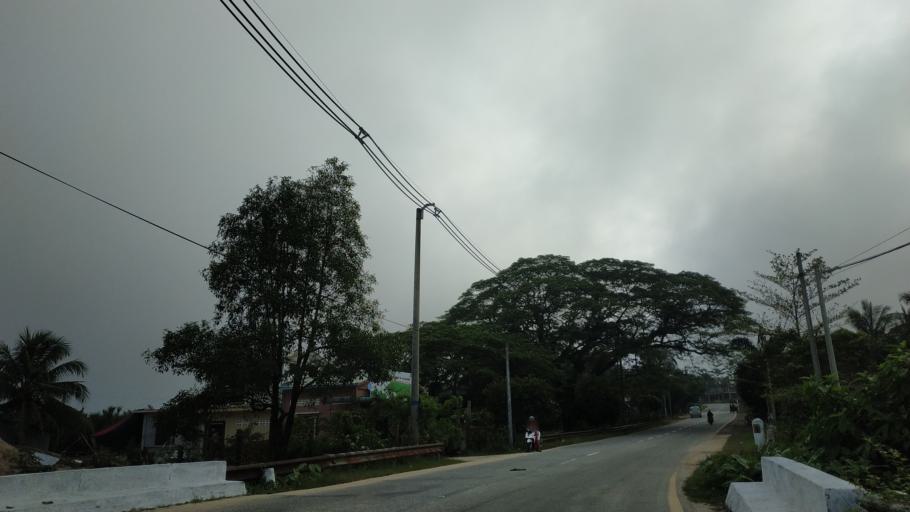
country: MM
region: Tanintharyi
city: Dawei
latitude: 14.1124
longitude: 98.1949
